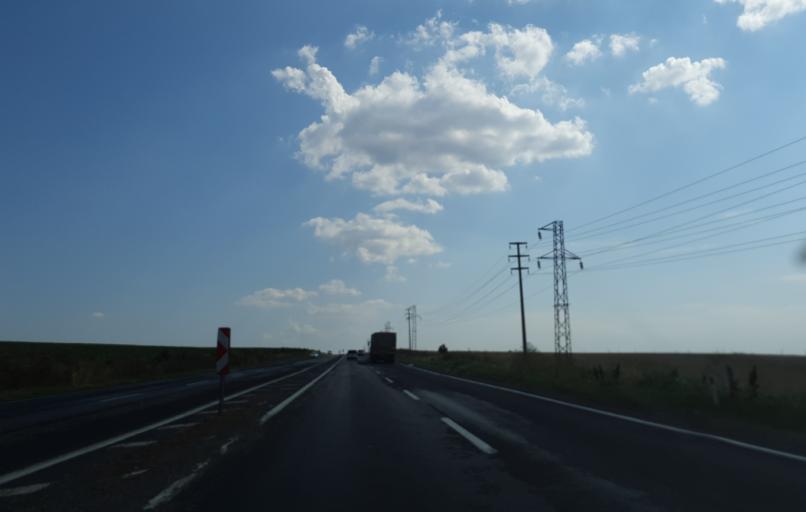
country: TR
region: Kirklareli
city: Buyukkaristiran
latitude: 41.2604
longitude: 27.5470
